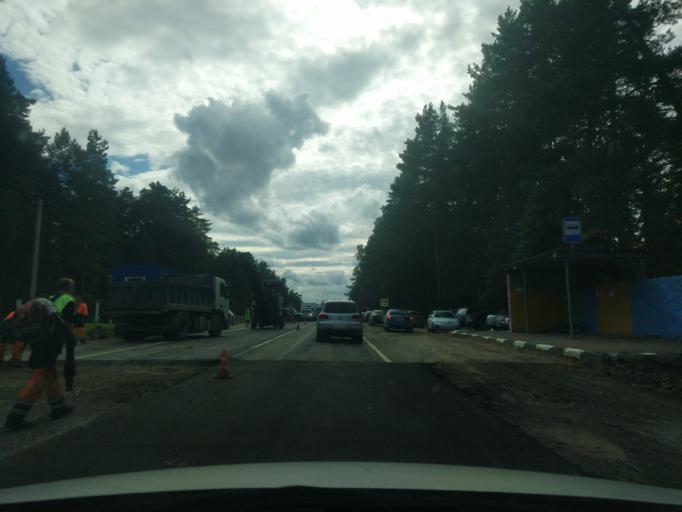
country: RU
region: Jaroslavl
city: Levashevo
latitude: 57.6758
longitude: 40.5879
